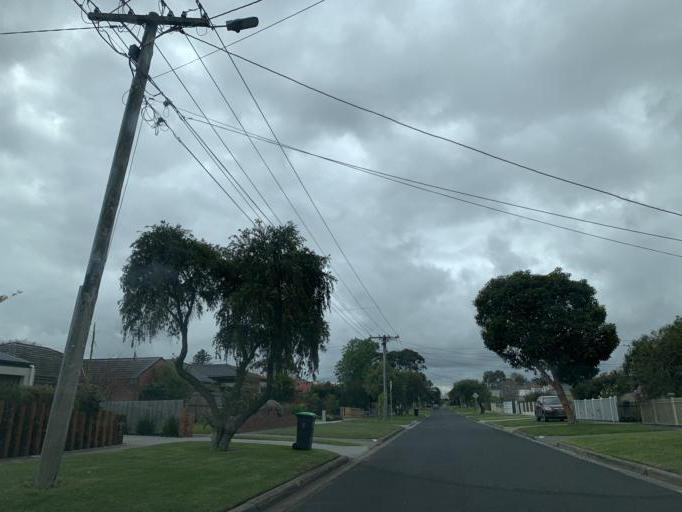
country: AU
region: Victoria
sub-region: Kingston
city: Parkdale
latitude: -37.9892
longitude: 145.0765
